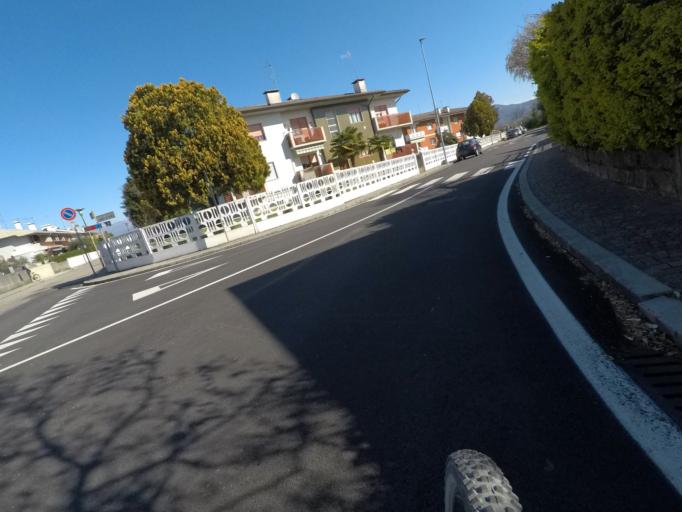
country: IT
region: Friuli Venezia Giulia
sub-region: Provincia di Udine
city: Remanzacco
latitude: 46.0887
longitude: 13.3260
